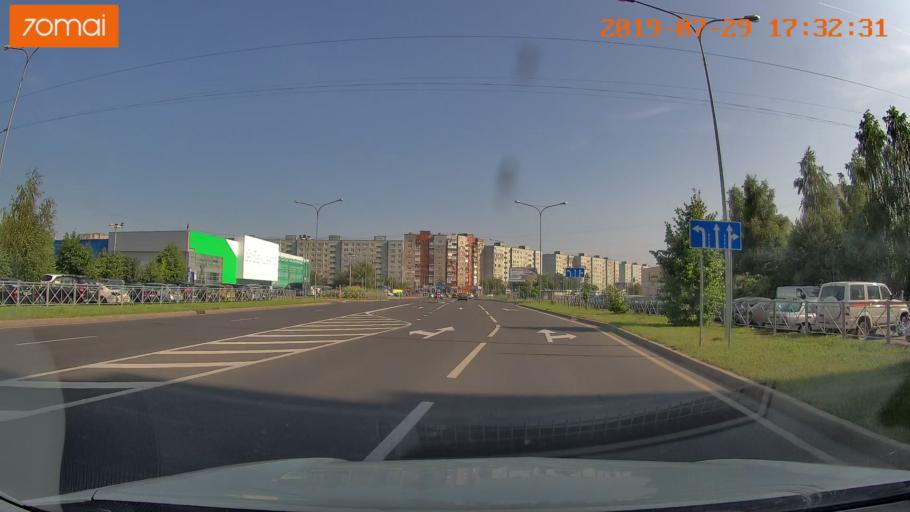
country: RU
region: Kaliningrad
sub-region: Gorod Kaliningrad
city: Kaliningrad
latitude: 54.7419
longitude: 20.4935
